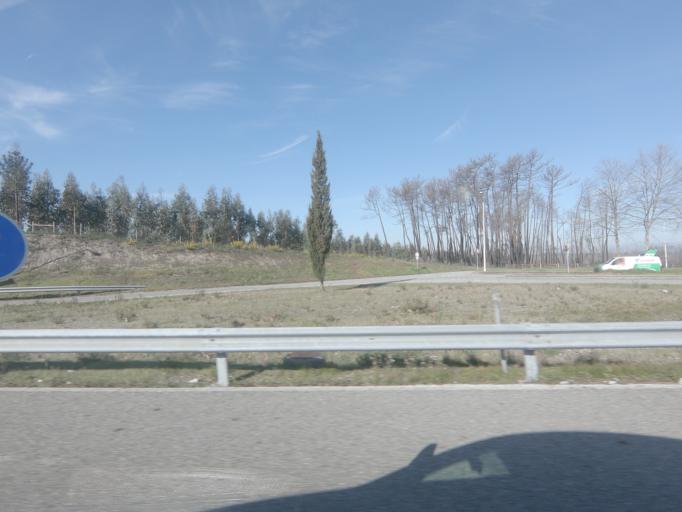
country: PT
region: Aveiro
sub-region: Oliveira do Bairro
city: Oia
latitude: 40.5504
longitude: -8.5601
